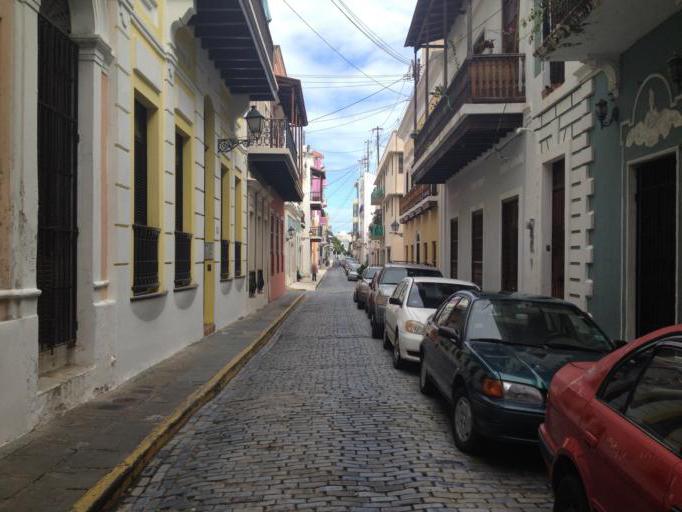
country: PR
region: San Juan
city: San Juan
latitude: 18.4669
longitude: -66.1162
